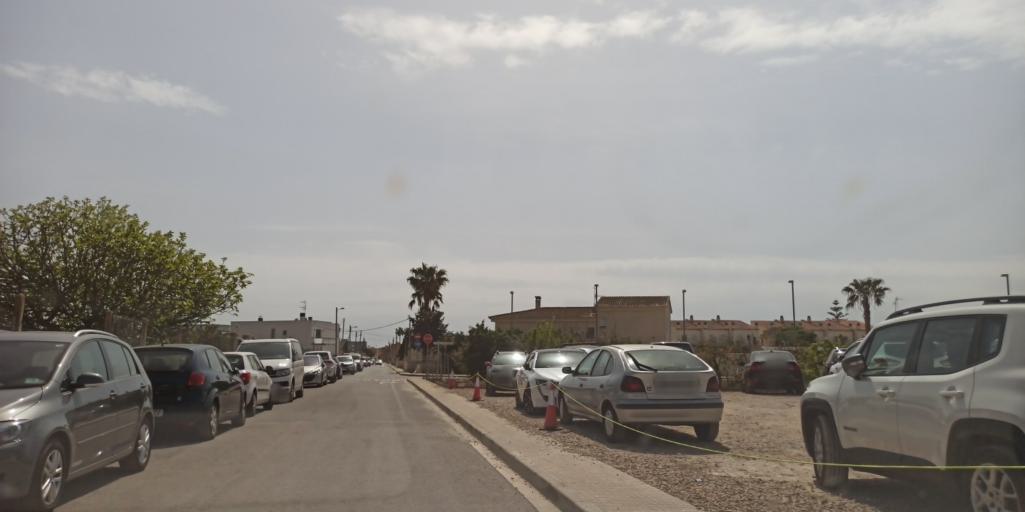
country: ES
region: Catalonia
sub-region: Provincia de Tarragona
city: Deltebre
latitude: 40.7116
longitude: 0.7180
